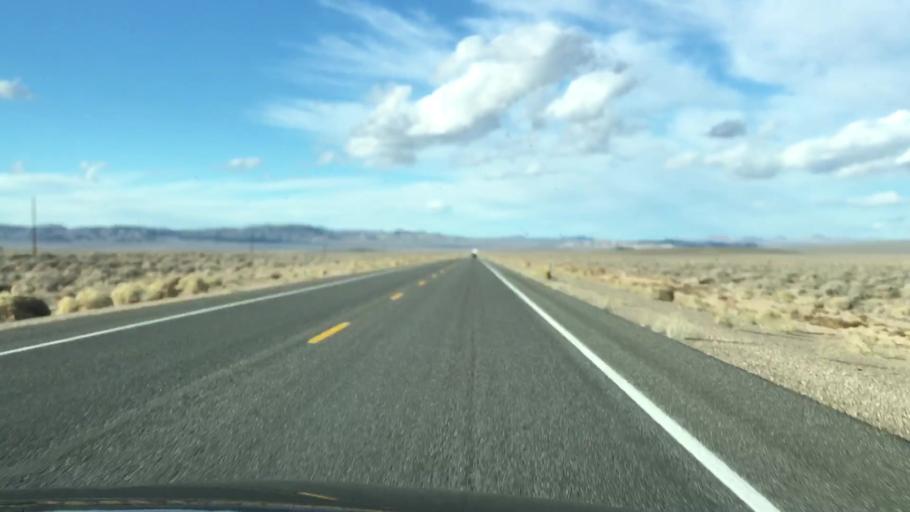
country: US
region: Nevada
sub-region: Esmeralda County
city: Goldfield
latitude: 37.4019
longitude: -117.1492
